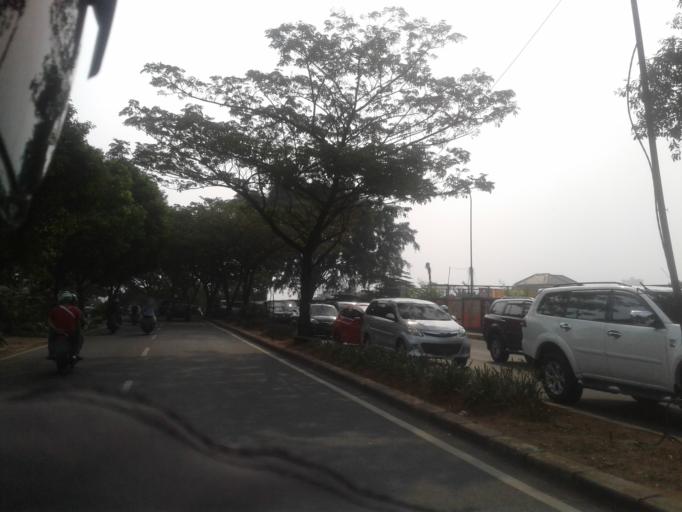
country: ID
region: West Java
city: Depok
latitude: -6.3793
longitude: 106.8480
